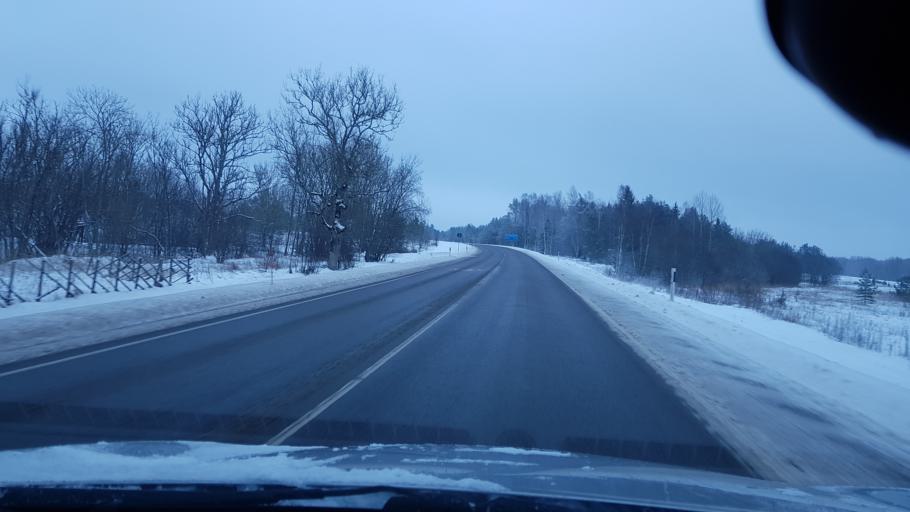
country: EE
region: Harju
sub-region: Keila linn
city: Keila
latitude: 59.3378
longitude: 24.2743
